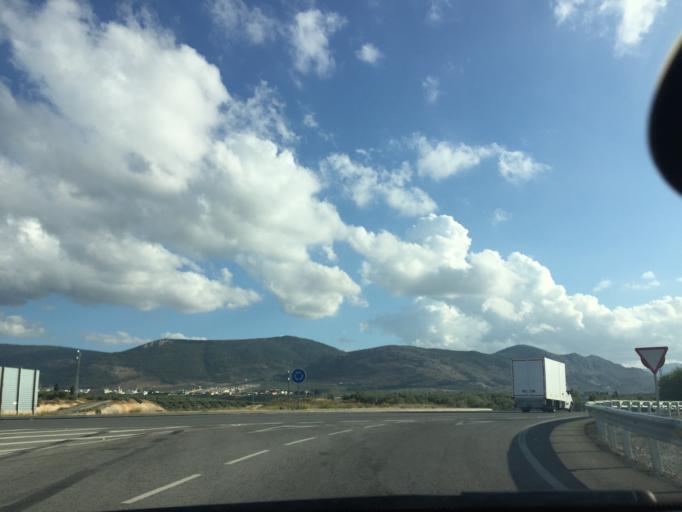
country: ES
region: Andalusia
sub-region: Provincia de Jaen
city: Mancha Real
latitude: 37.8050
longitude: -3.6266
